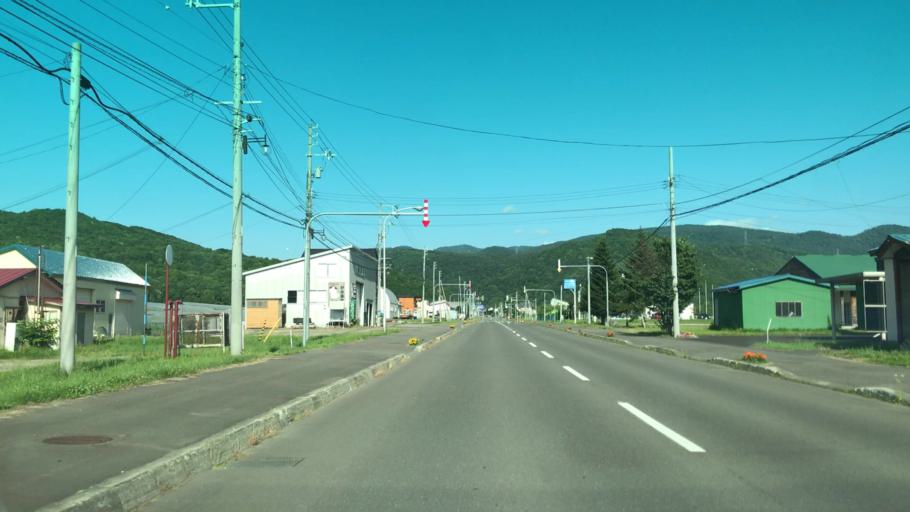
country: JP
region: Hokkaido
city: Yoichi
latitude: 43.0508
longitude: 140.8338
